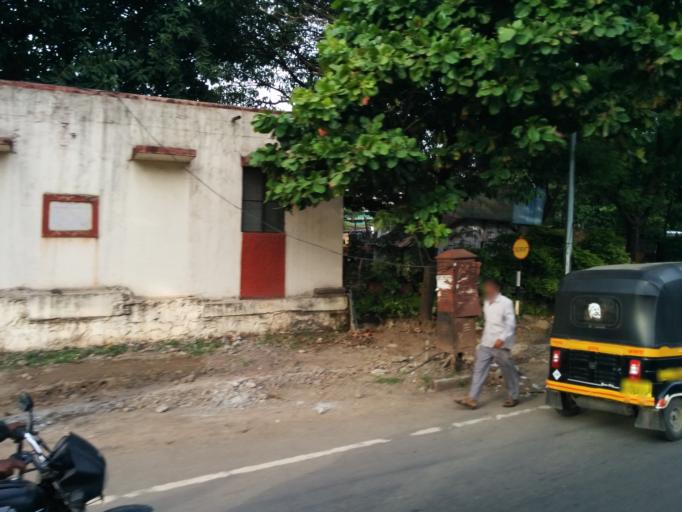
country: IN
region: Maharashtra
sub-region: Pune Division
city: Pune
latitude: 18.5064
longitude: 73.8243
